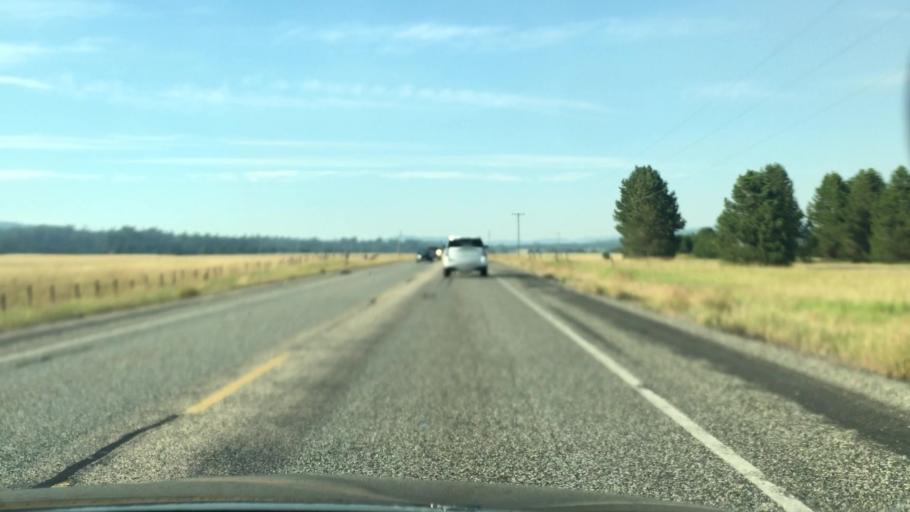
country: US
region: Idaho
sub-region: Valley County
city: Cascade
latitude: 44.3418
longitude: -116.0291
